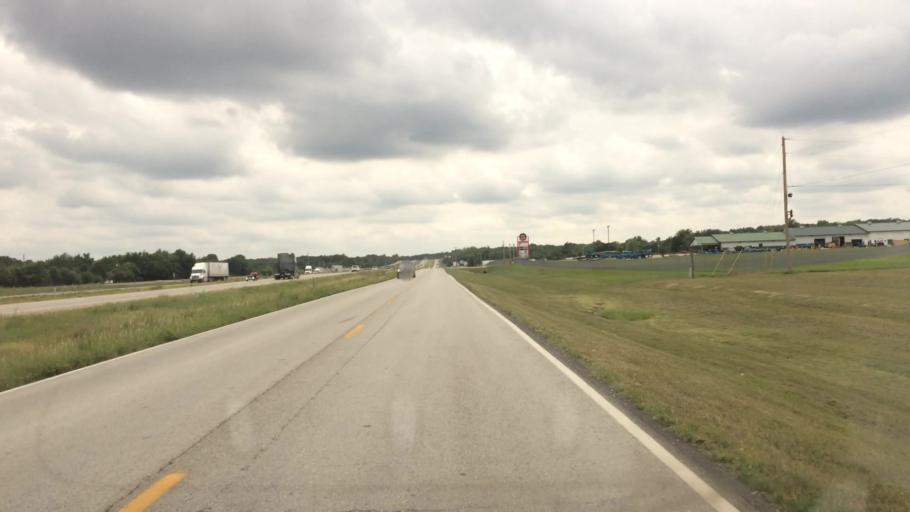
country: US
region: Missouri
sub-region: Greene County
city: Strafford
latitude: 37.2941
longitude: -93.0243
